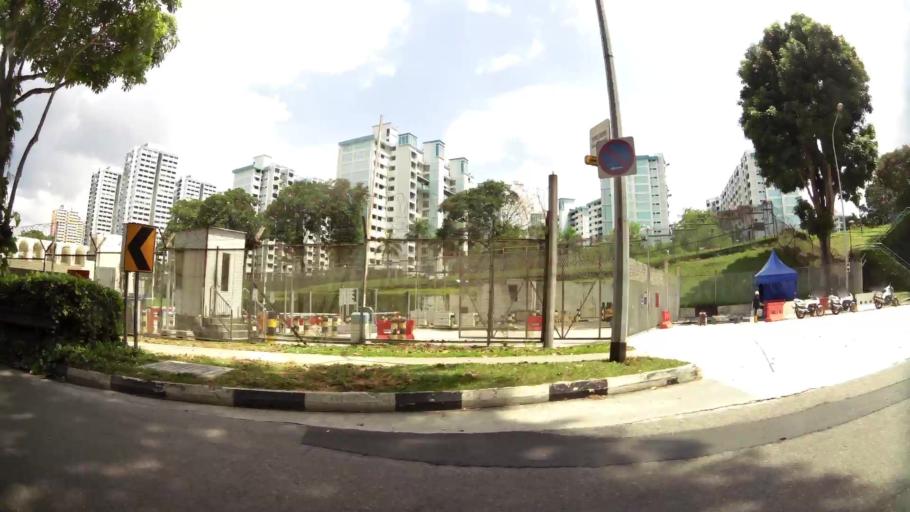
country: MY
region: Johor
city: Johor Bahru
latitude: 1.4430
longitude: 103.7709
